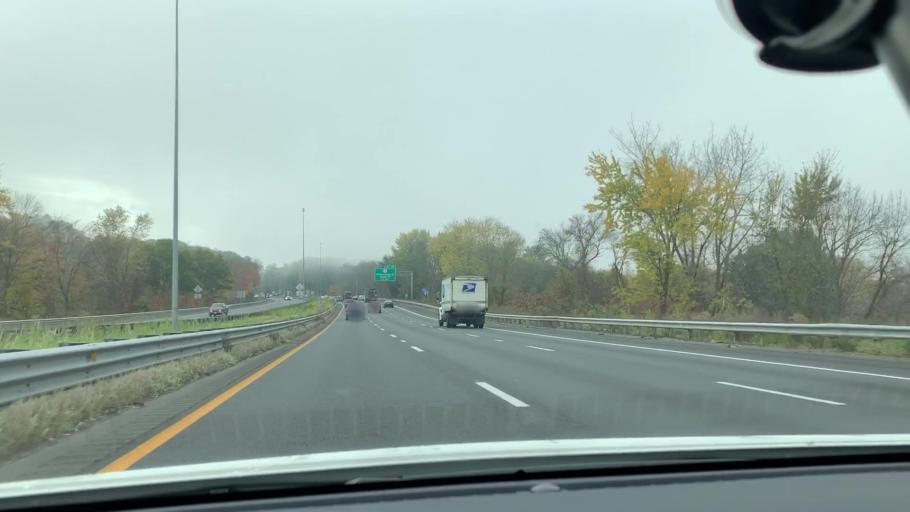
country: US
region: Massachusetts
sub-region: Hampden County
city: Longmeadow
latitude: 42.0323
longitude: -72.5898
